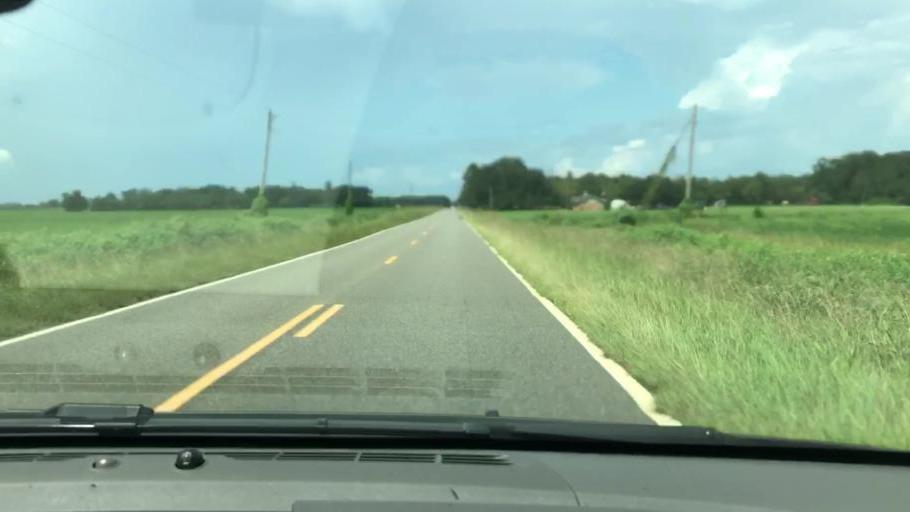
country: US
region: Georgia
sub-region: Seminole County
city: Donalsonville
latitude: 31.1038
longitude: -84.9960
